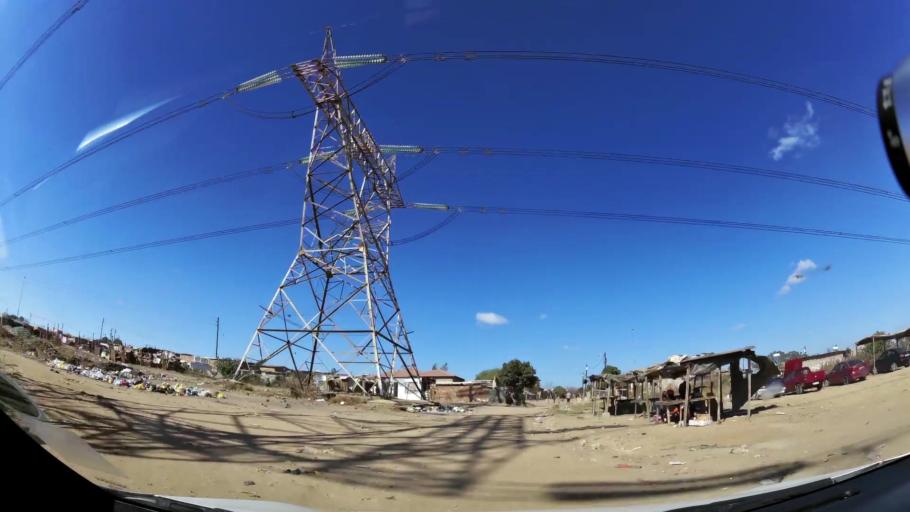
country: ZA
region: Gauteng
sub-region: City of Johannesburg Metropolitan Municipality
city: Midrand
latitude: -25.9201
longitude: 28.0983
